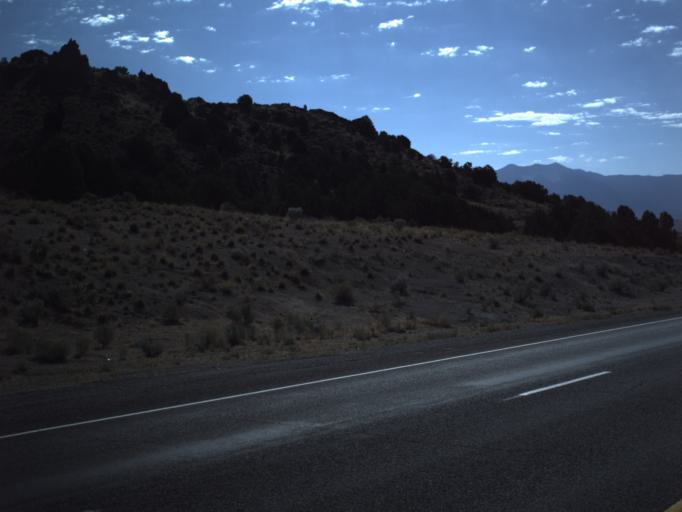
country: US
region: Utah
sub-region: Utah County
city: Genola
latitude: 39.9579
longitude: -112.0361
